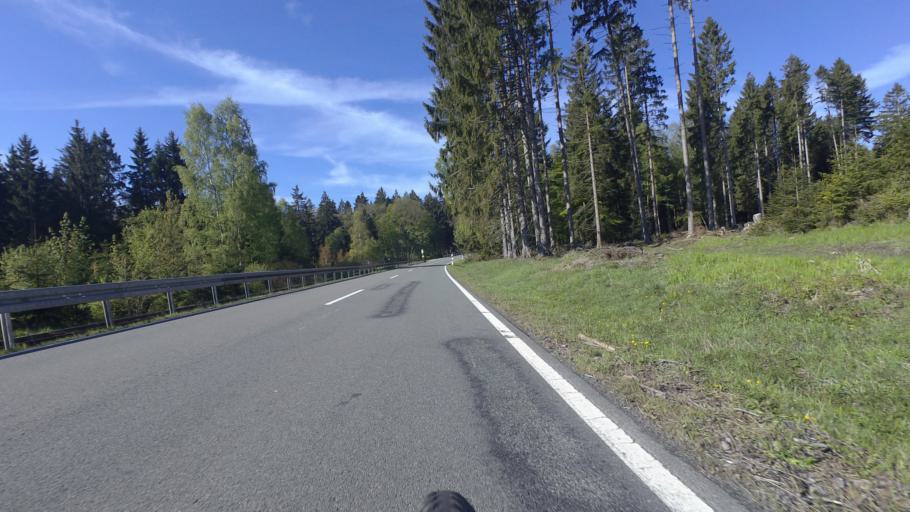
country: DE
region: Saxony-Anhalt
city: Benneckenstein
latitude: 51.7578
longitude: 10.7141
